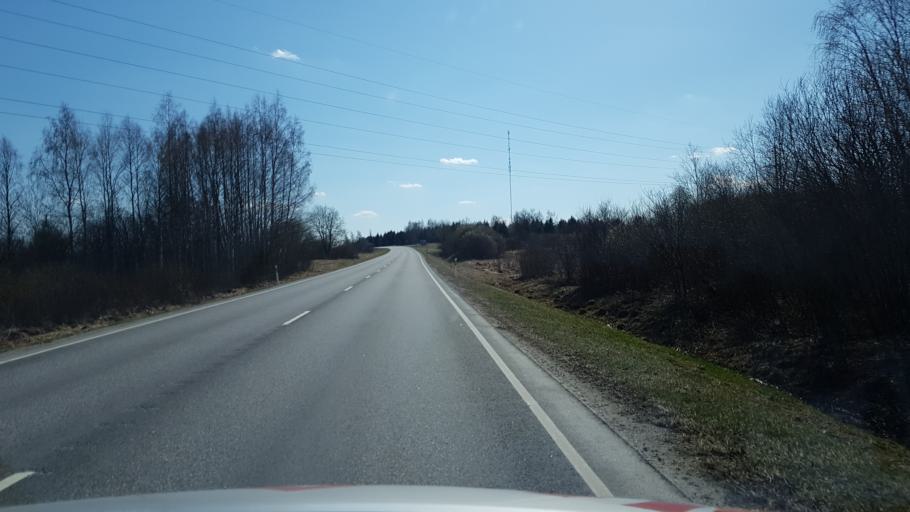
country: EE
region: Jogevamaa
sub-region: Mustvee linn
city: Mustvee
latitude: 58.6753
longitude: 26.7964
